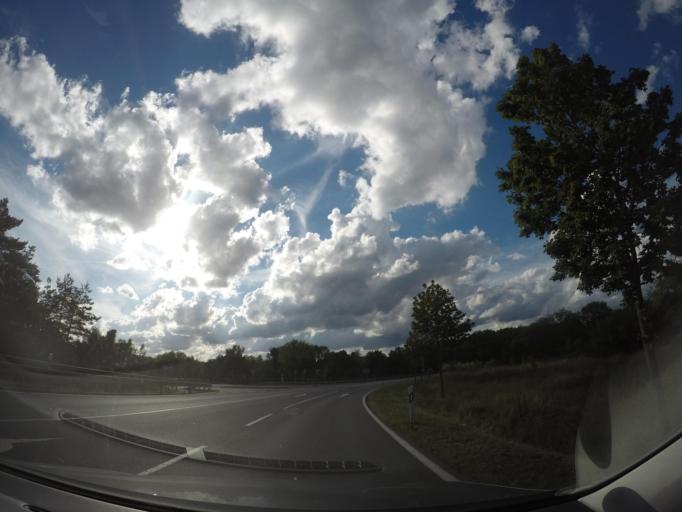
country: DE
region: Saxony-Anhalt
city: Bulstringen
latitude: 52.3014
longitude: 11.3694
